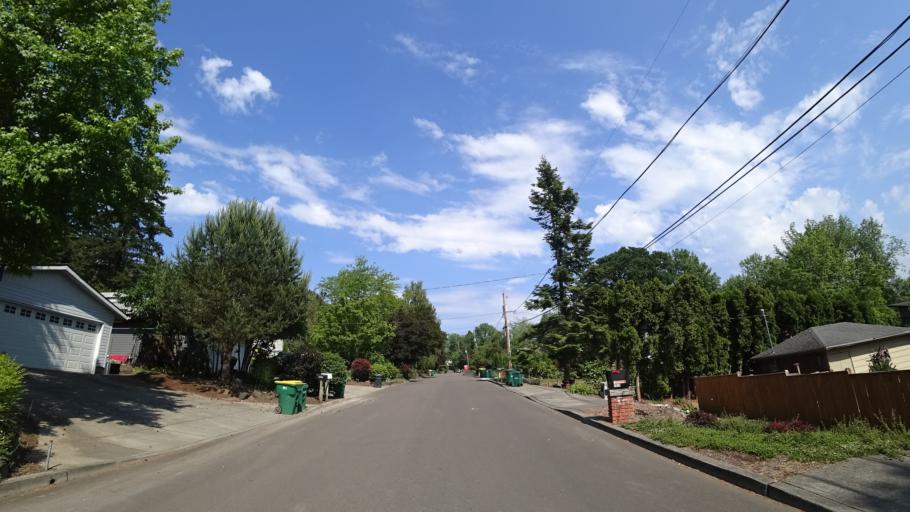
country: US
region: Oregon
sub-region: Washington County
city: Metzger
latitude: 45.4525
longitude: -122.7469
